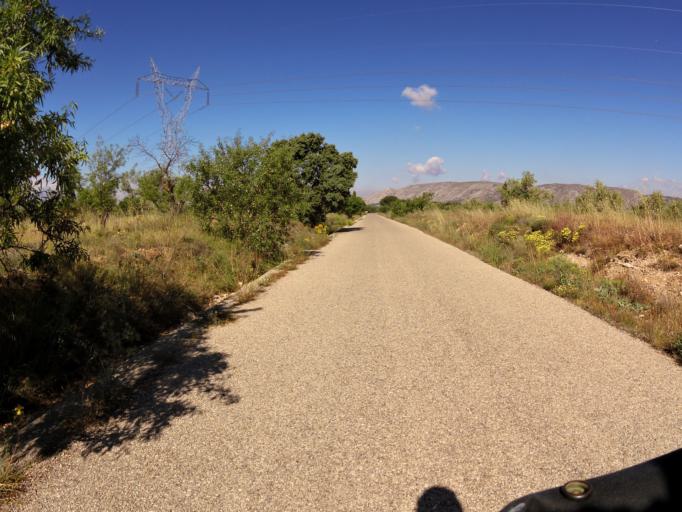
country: ES
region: Valencia
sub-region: Provincia de Alicante
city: Biar
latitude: 38.6318
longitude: -0.7948
